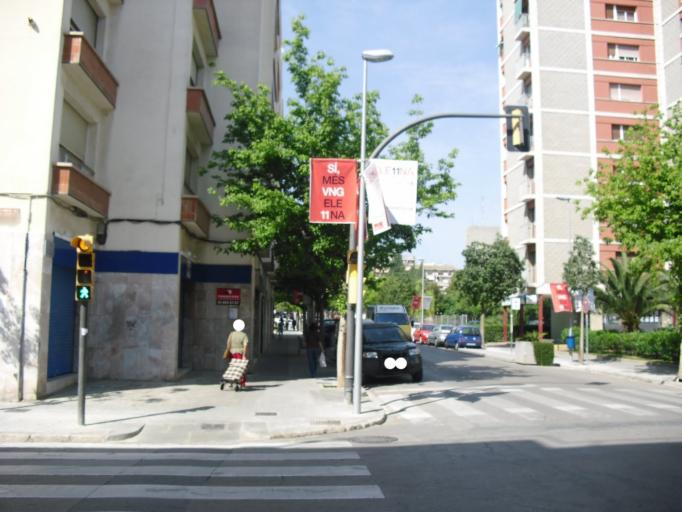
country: ES
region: Catalonia
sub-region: Provincia de Barcelona
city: Vilanova i la Geltru
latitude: 41.2210
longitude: 1.7151
